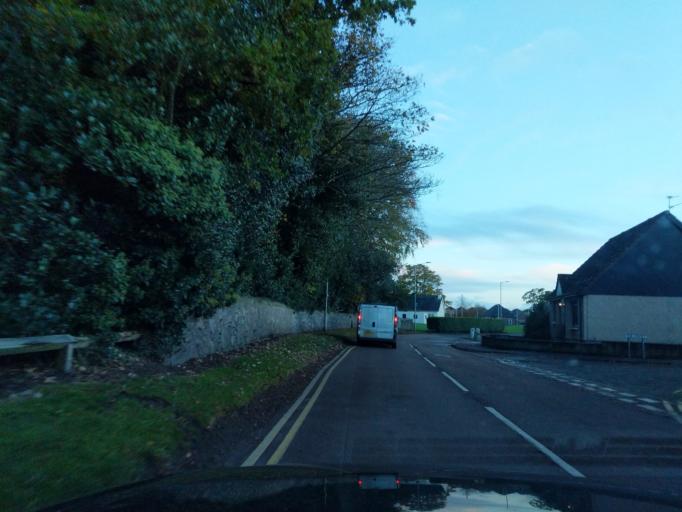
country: GB
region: Scotland
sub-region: Fife
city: Leuchars
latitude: 56.3806
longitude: -2.8815
